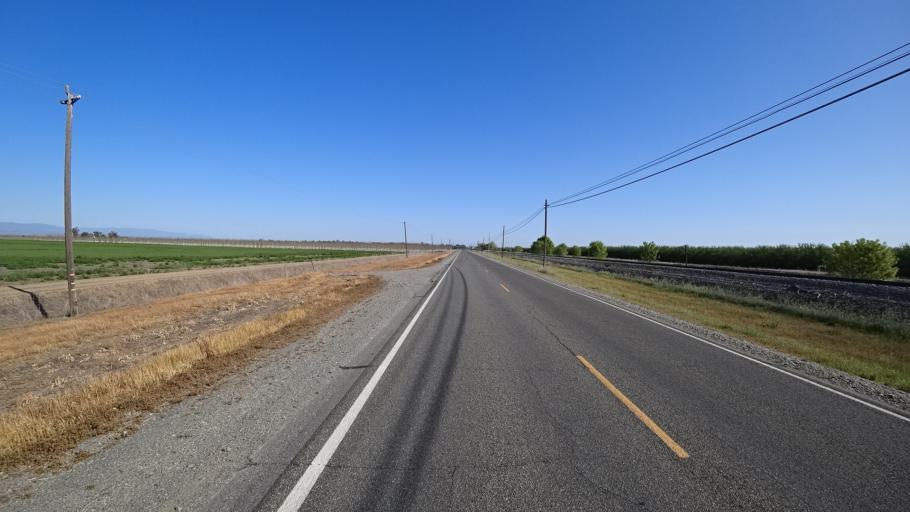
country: US
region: California
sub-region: Glenn County
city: Willows
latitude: 39.5623
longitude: -122.1937
